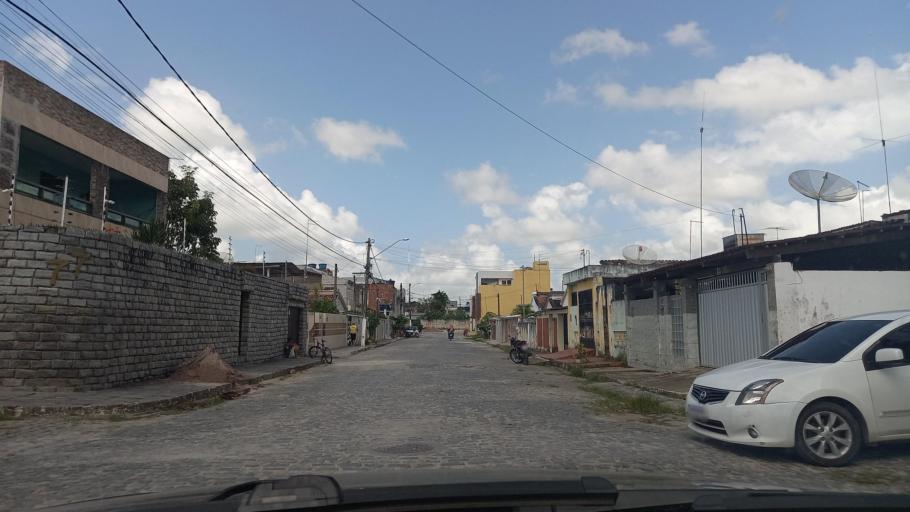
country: BR
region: Pernambuco
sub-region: Goiana
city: Goiana
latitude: -7.5635
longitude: -34.9972
